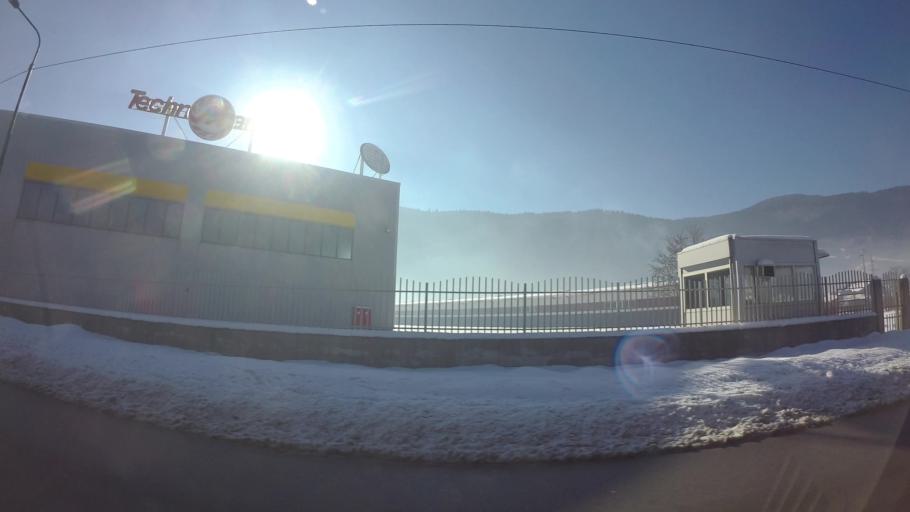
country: BA
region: Federation of Bosnia and Herzegovina
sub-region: Kanton Sarajevo
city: Sarajevo
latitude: 43.7937
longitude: 18.3270
